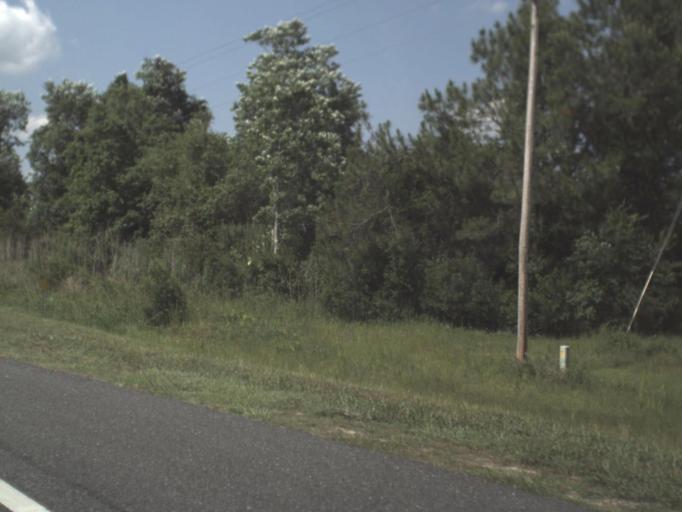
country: US
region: Florida
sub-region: Alachua County
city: Waldo
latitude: 29.7587
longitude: -82.1410
